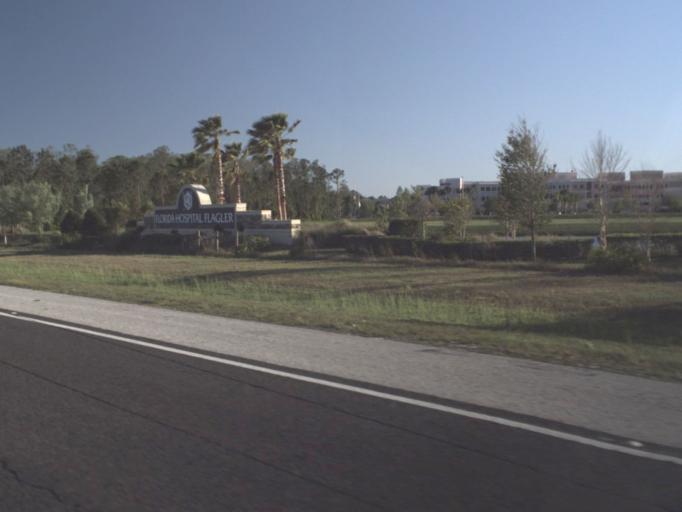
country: US
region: Florida
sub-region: Flagler County
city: Flagler Beach
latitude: 29.4833
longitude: -81.1867
